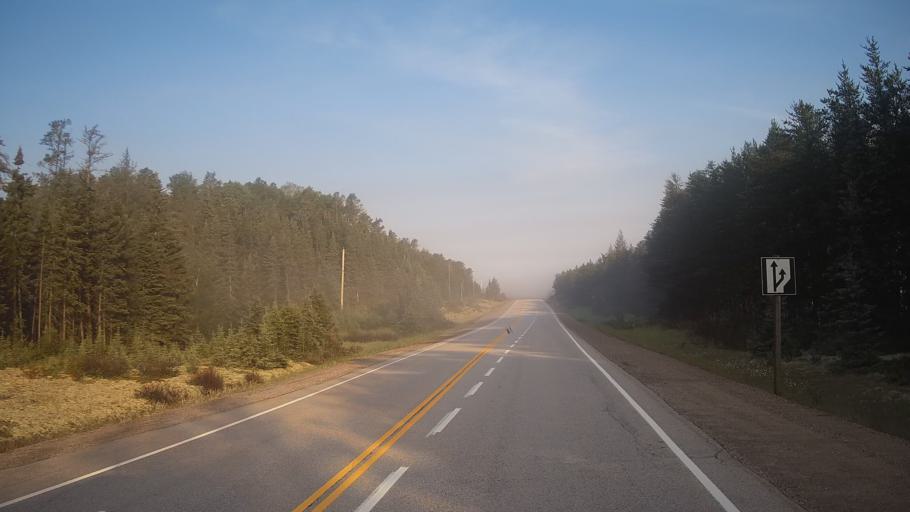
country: CA
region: Ontario
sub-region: Rainy River District
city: Atikokan
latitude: 49.2588
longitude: -91.1981
